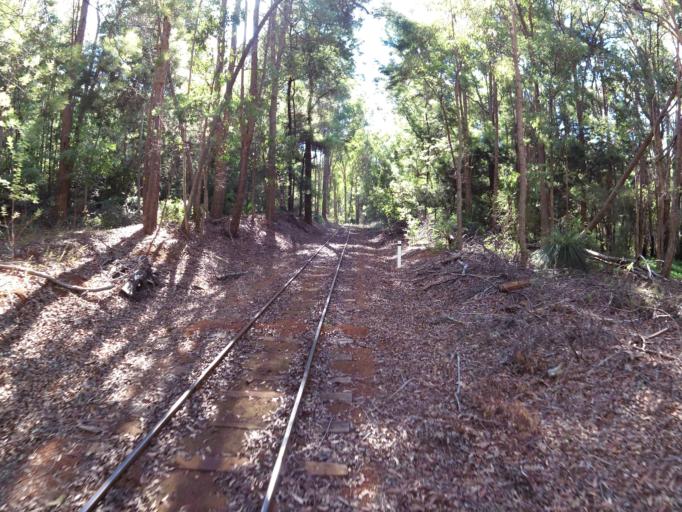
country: AU
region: Western Australia
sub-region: Waroona
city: Waroona
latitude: -32.7171
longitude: 116.0974
